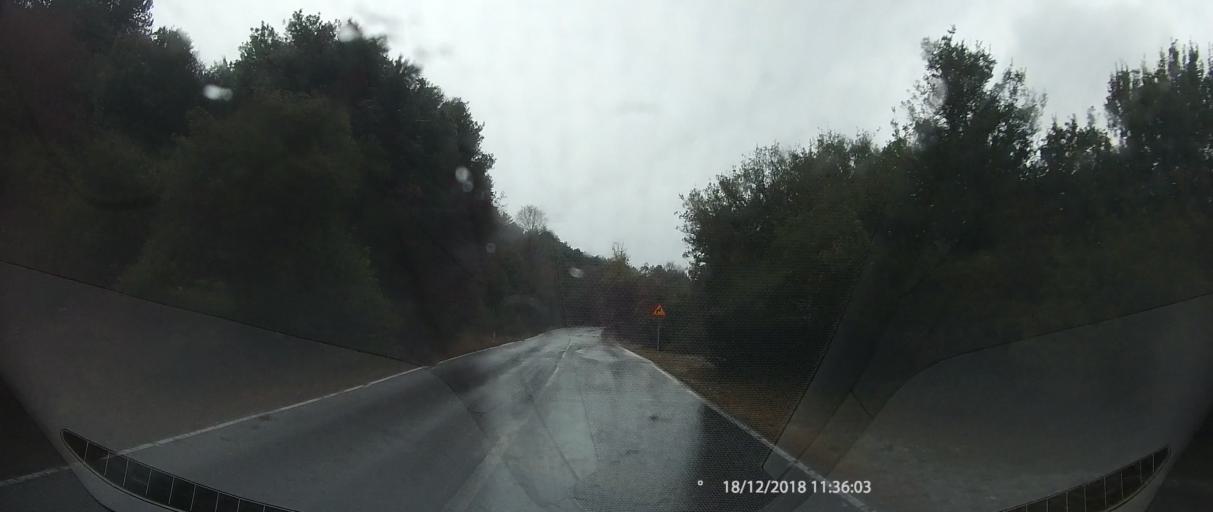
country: GR
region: Central Macedonia
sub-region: Nomos Pierias
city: Litochoro
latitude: 40.1142
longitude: 22.4839
